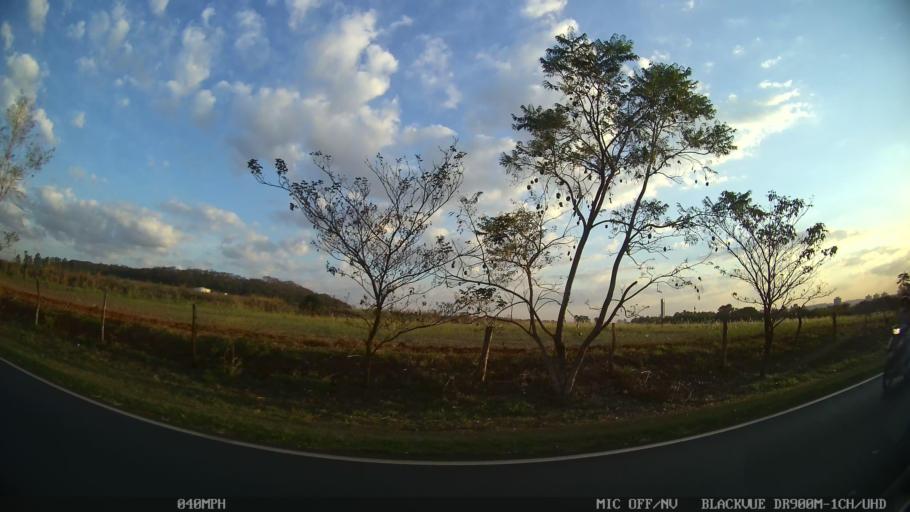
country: BR
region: Sao Paulo
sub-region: Ribeirao Preto
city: Ribeirao Preto
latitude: -21.1557
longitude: -47.7757
